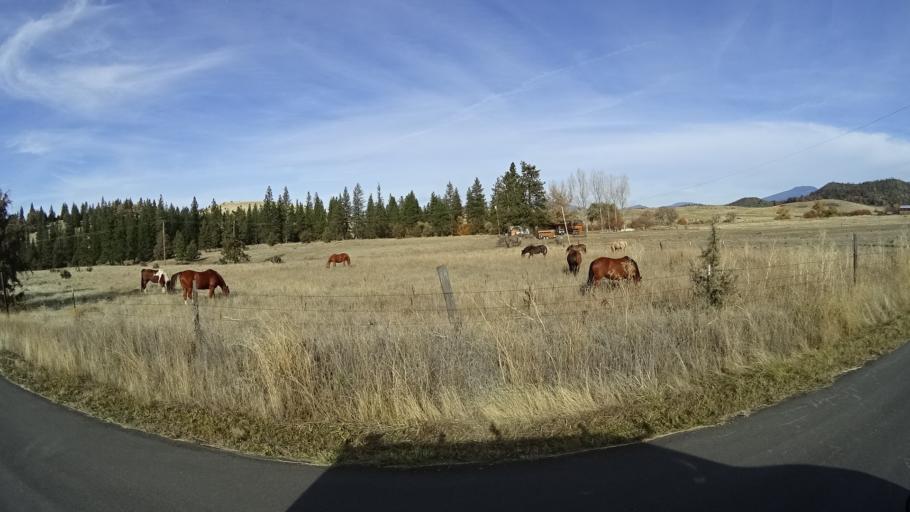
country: US
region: California
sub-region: Siskiyou County
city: Weed
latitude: 41.4652
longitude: -122.4028
